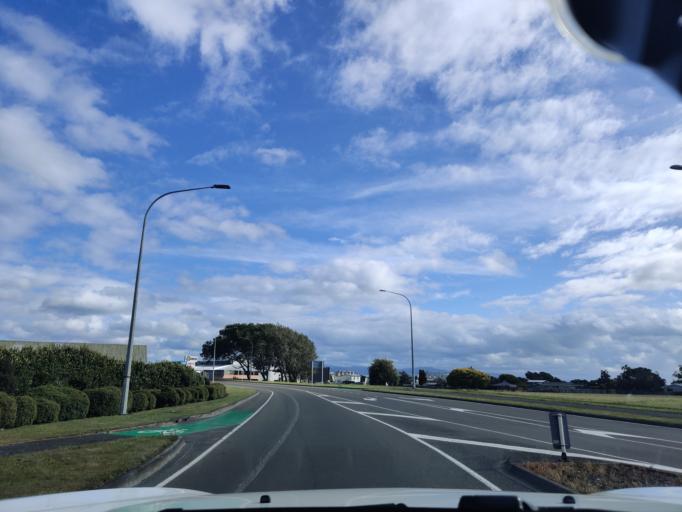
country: NZ
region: Manawatu-Wanganui
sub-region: Palmerston North City
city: Palmerston North
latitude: -40.3249
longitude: 175.6254
